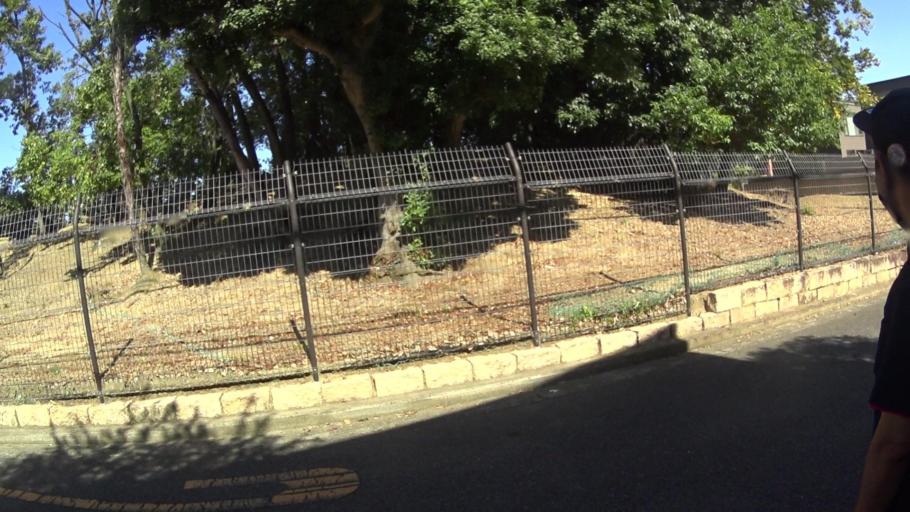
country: JP
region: Osaka
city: Takaishi
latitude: 34.5011
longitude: 135.4353
